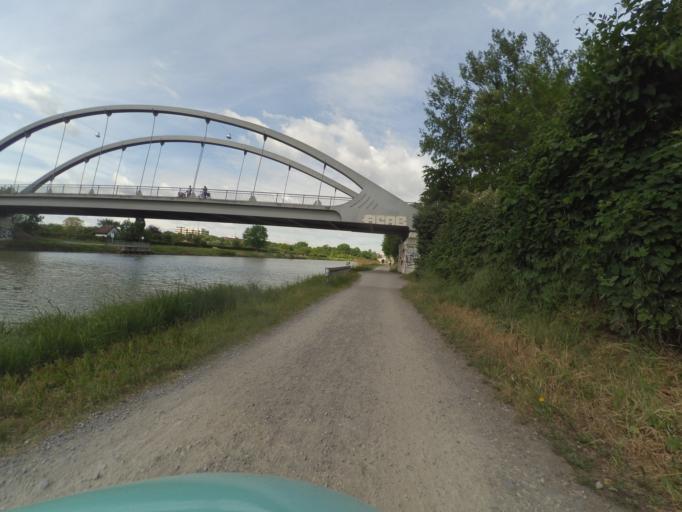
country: DE
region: Lower Saxony
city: Hannover
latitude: 52.4052
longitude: 9.7548
